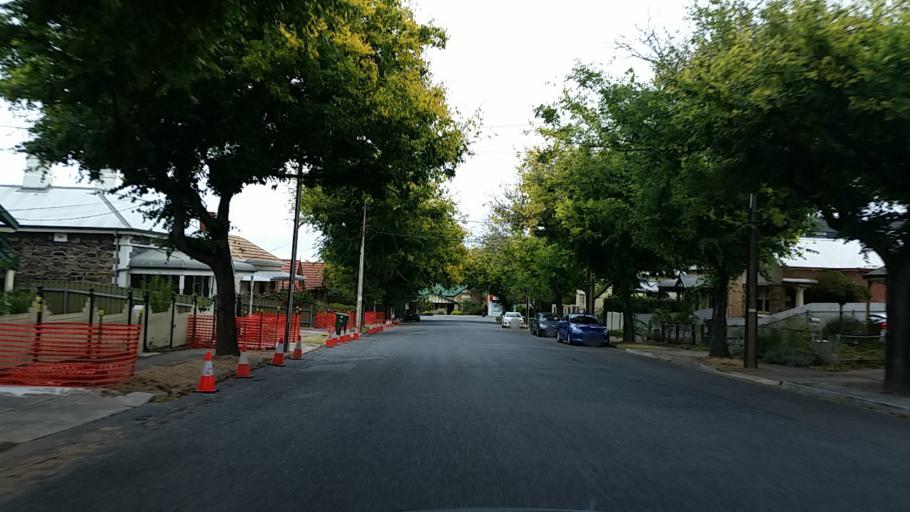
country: AU
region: South Australia
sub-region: Prospect
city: Prospect
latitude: -34.8800
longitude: 138.5949
